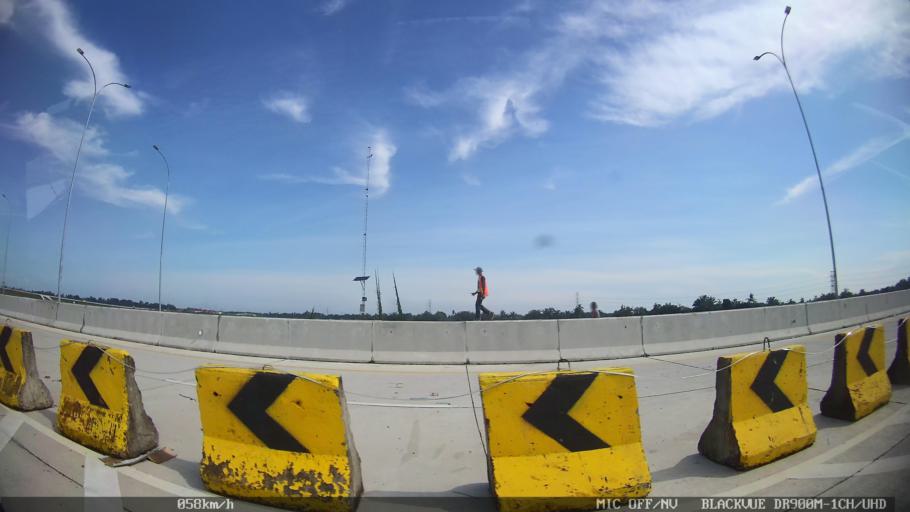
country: ID
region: North Sumatra
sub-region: Kabupaten Langkat
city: Stabat
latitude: 3.7133
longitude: 98.5004
